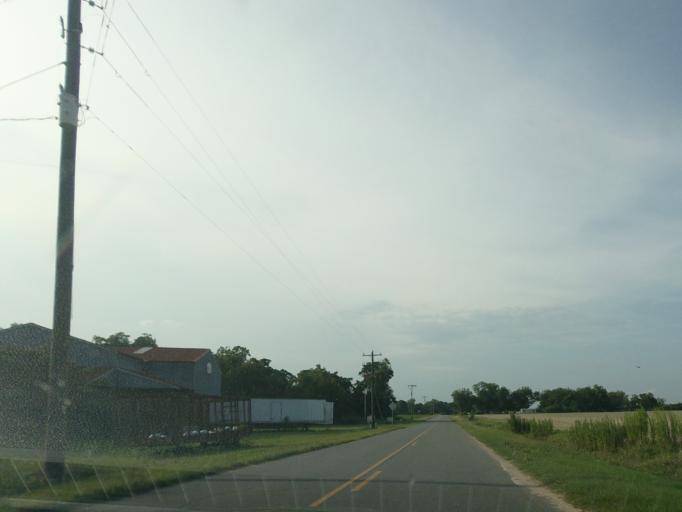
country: US
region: Georgia
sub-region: Bleckley County
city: Cochran
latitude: 32.5160
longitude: -83.3054
